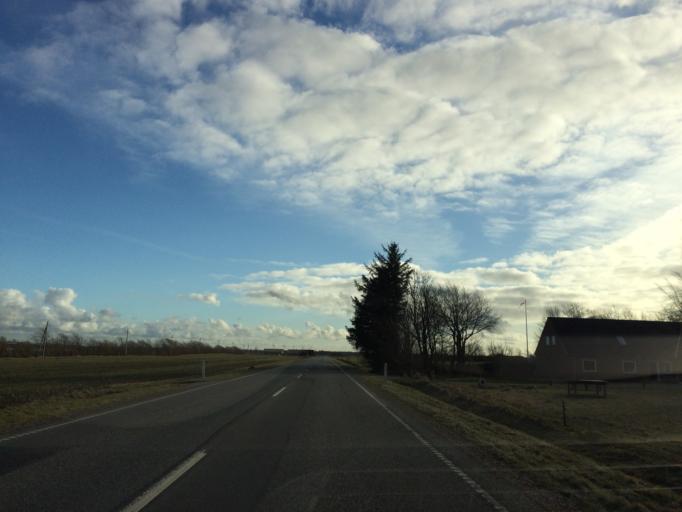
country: DK
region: Central Jutland
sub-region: Lemvig Kommune
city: Lemvig
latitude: 56.4452
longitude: 8.2954
